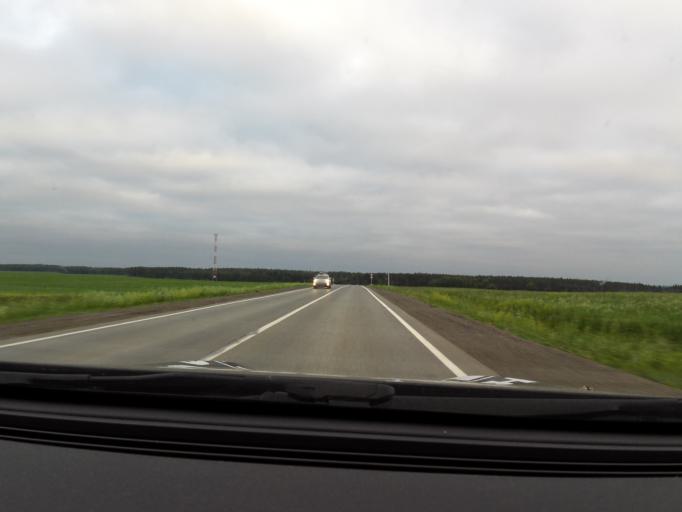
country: RU
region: Perm
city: Zyukayka
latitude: 58.3047
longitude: 54.7534
